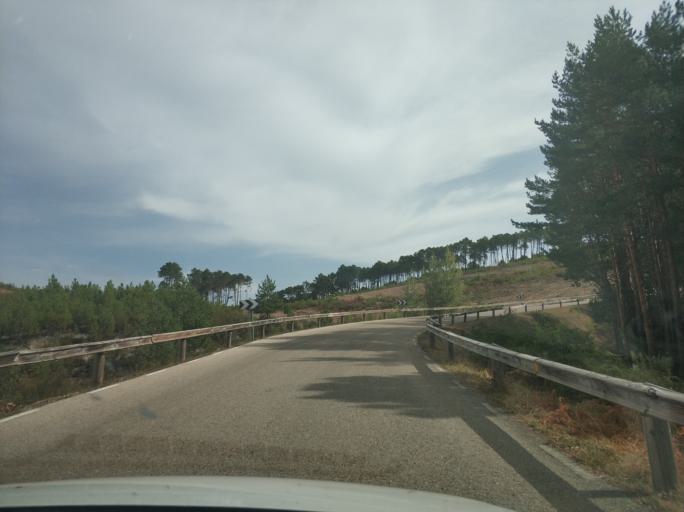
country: ES
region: Castille and Leon
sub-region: Provincia de Soria
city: Navaleno
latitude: 41.8506
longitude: -2.9857
